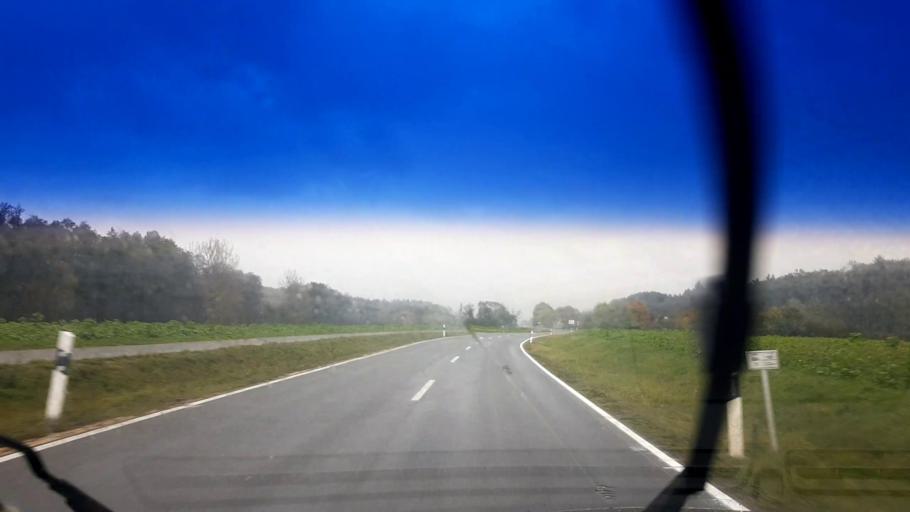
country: DE
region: Bavaria
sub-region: Upper Franconia
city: Memmelsdorf
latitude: 49.9205
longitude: 10.9681
